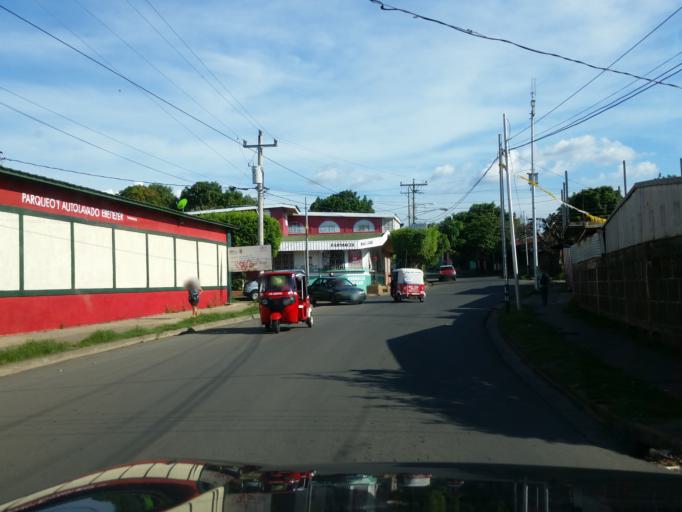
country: NI
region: Managua
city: Managua
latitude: 12.1080
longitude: -86.2236
